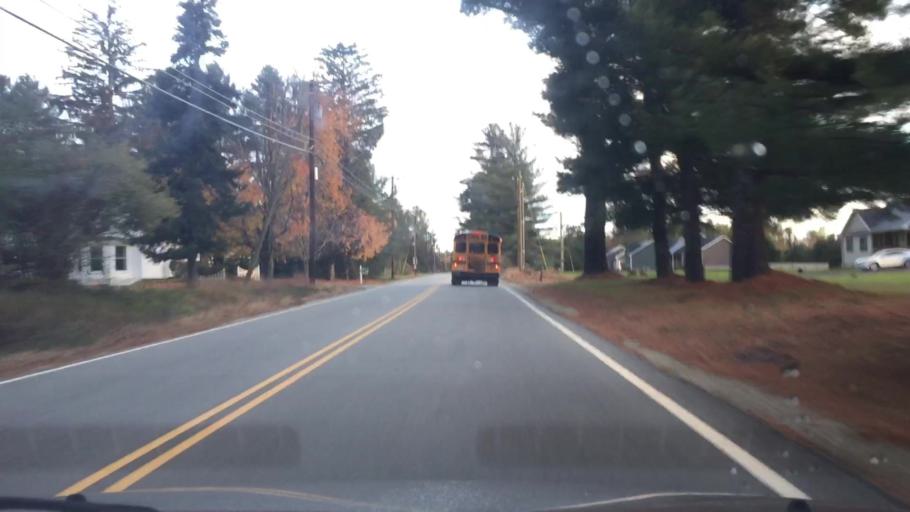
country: US
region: New Hampshire
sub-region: Cheshire County
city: Swanzey
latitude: 42.8549
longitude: -72.2782
